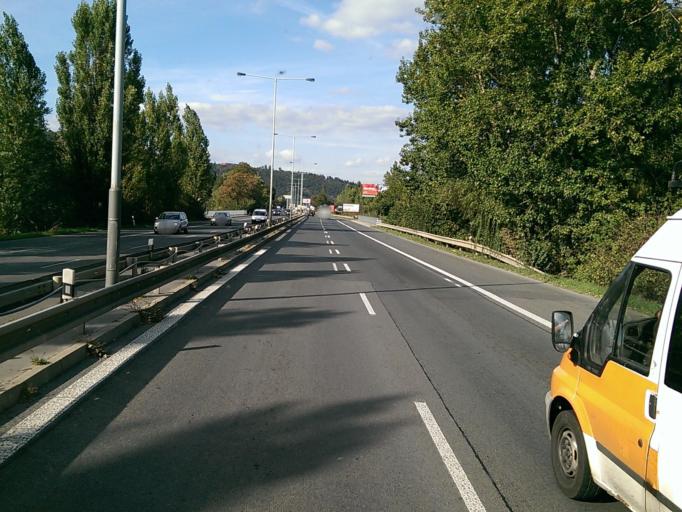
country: CZ
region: Praha
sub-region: Praha 12
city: Modrany
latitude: 50.0082
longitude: 14.3948
